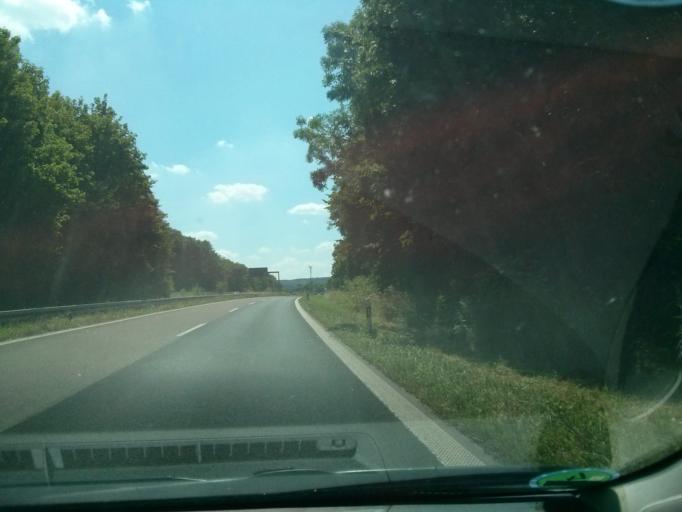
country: DE
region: North Rhine-Westphalia
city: Meckenheim
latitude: 50.5946
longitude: 7.0315
